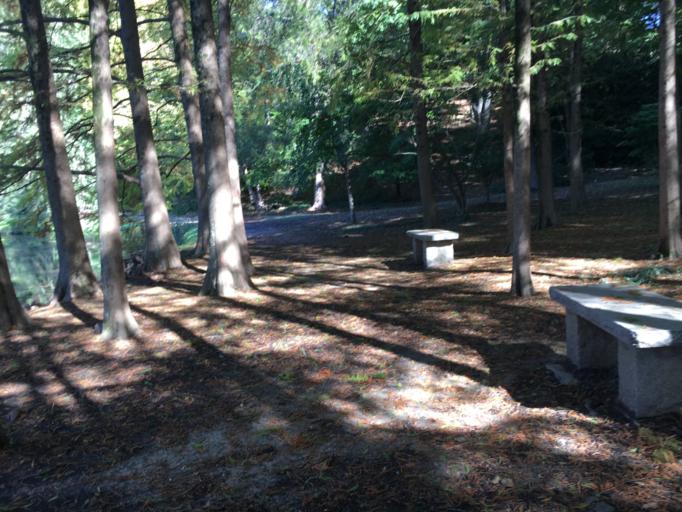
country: US
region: Virginia
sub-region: City of Richmond
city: Richmond
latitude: 37.5322
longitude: -77.4758
